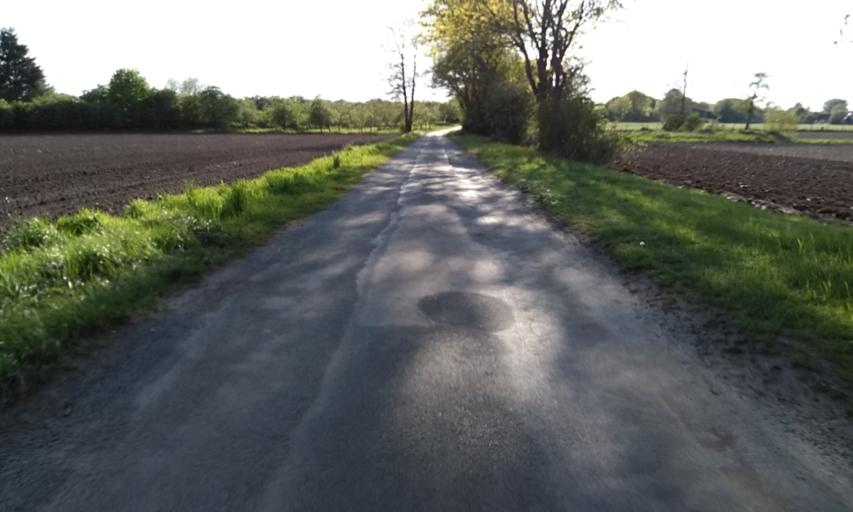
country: DE
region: Lower Saxony
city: Beckdorf
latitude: 53.4064
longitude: 9.6207
